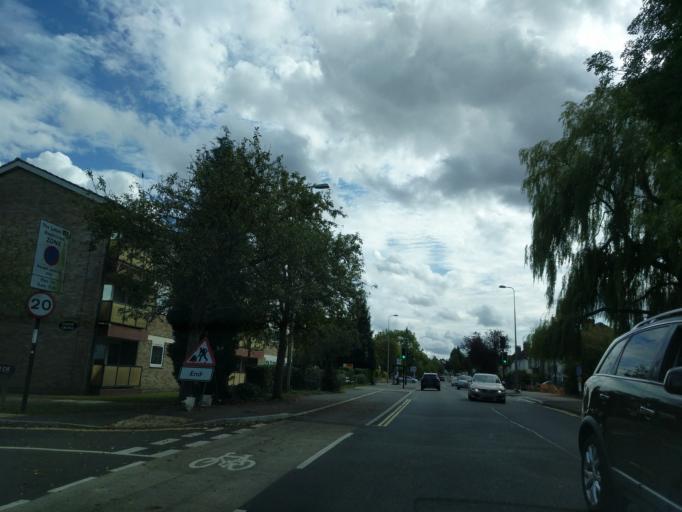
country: GB
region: England
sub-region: Oxfordshire
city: Oxford
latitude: 51.7646
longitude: -1.2263
